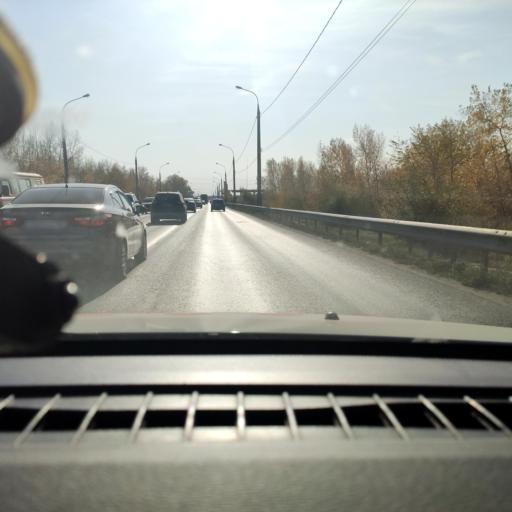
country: RU
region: Samara
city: Samara
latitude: 53.1474
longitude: 50.1838
